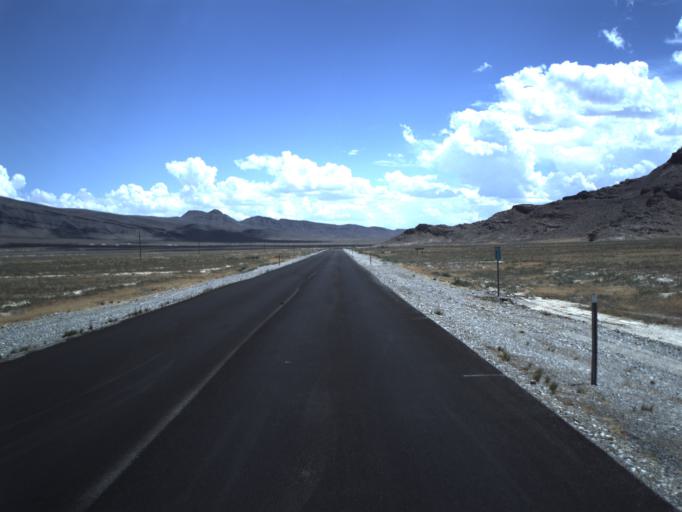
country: US
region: Utah
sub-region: Beaver County
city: Milford
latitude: 39.0702
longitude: -113.4610
